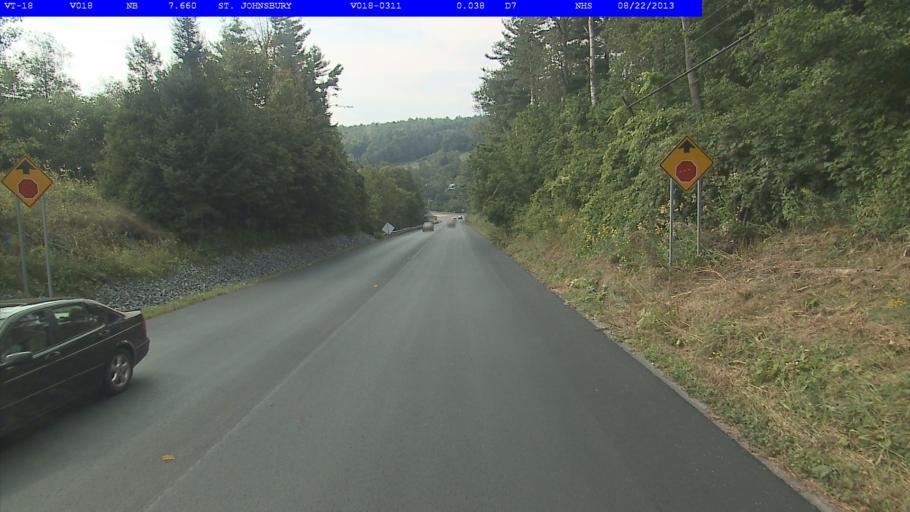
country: US
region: Vermont
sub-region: Caledonia County
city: St Johnsbury
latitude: 44.4278
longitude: -71.9599
